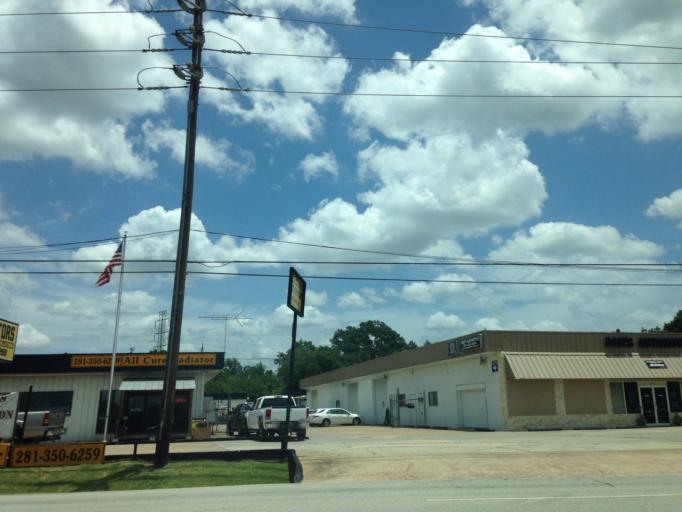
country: US
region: Texas
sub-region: Harris County
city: Spring
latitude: 30.0495
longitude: -95.4924
